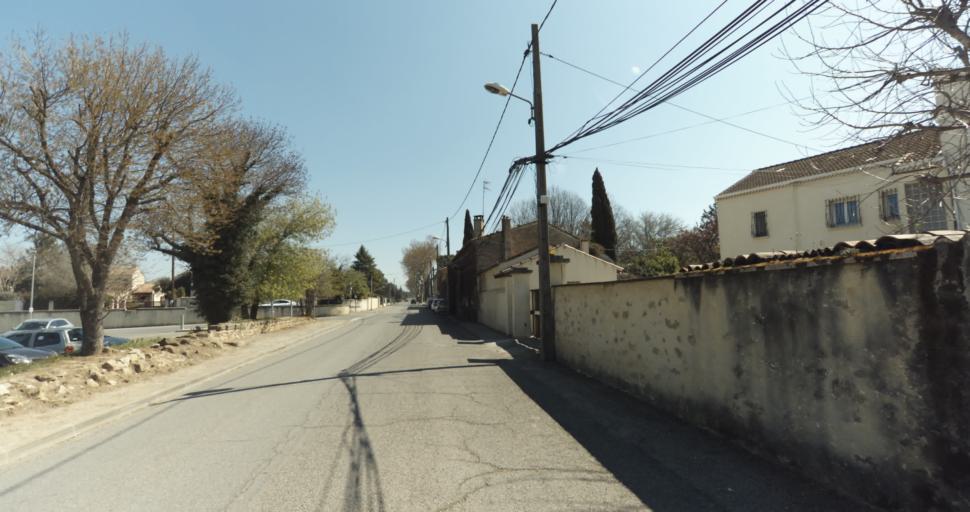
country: FR
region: Provence-Alpes-Cote d'Azur
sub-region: Departement des Bouches-du-Rhone
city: Pelissanne
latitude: 43.6252
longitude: 5.1550
